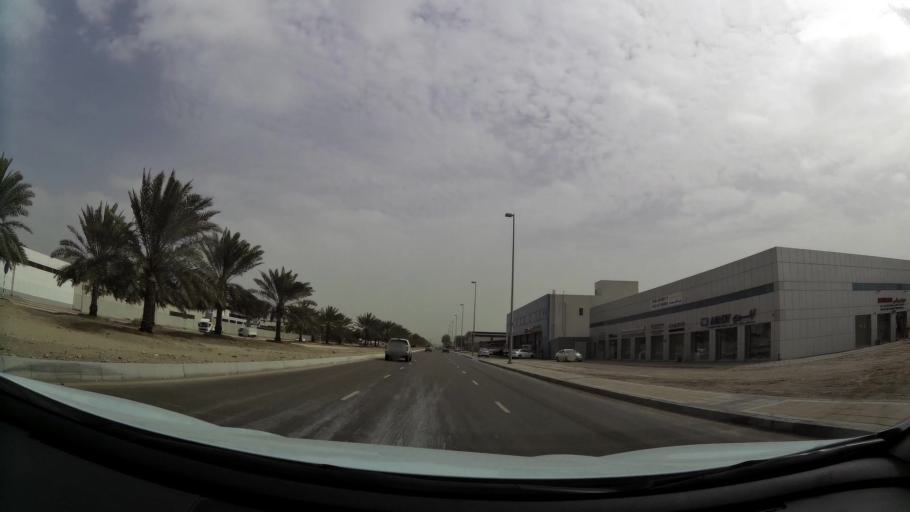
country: AE
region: Abu Dhabi
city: Abu Dhabi
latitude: 24.3719
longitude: 54.4823
